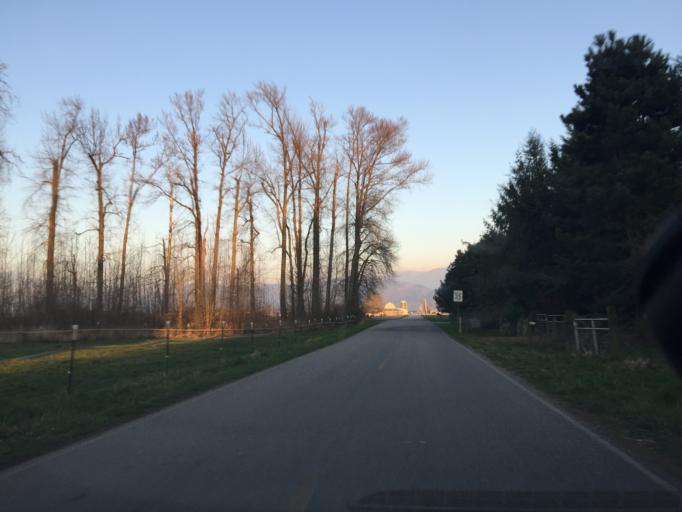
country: US
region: Washington
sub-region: Whatcom County
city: Sumas
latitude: 49.0001
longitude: -122.2506
